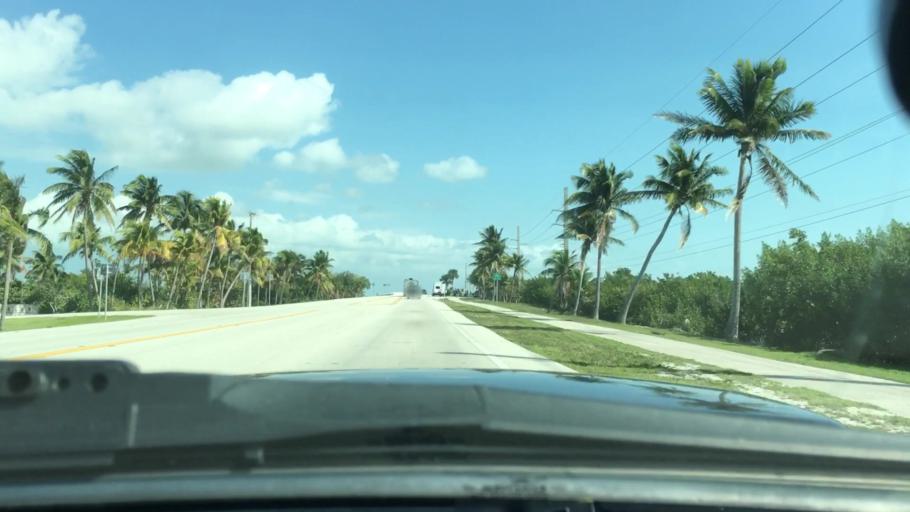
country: US
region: Florida
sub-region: Monroe County
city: Big Coppitt Key
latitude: 24.6024
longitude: -81.6454
